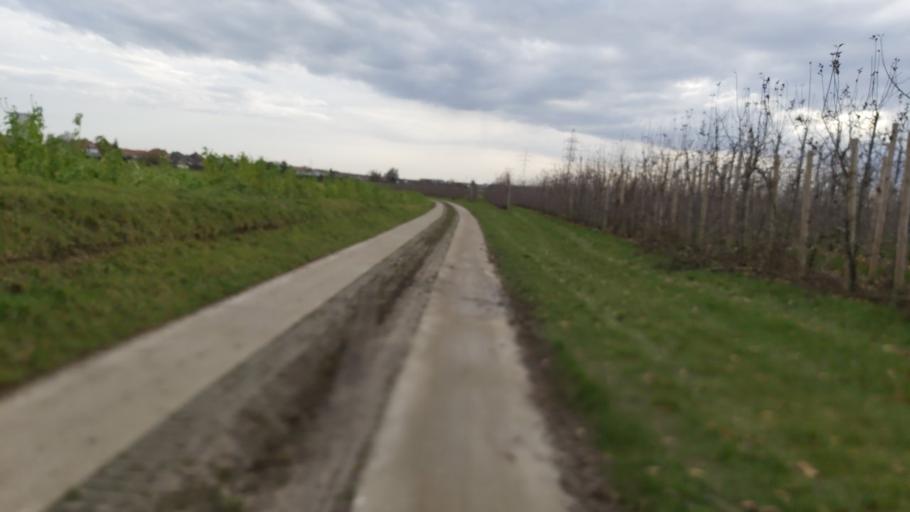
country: BE
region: Flanders
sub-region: Provincie Vlaams-Brabant
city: Tienen
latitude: 50.8288
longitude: 4.9181
